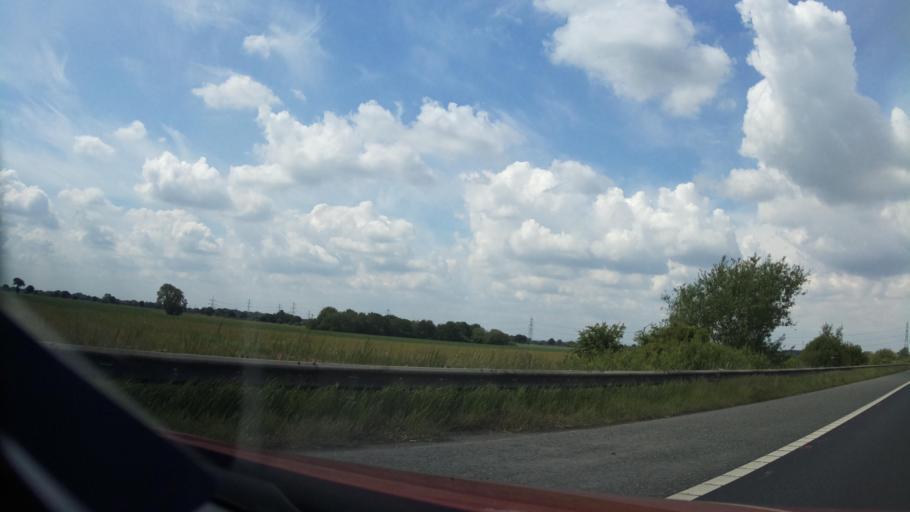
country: GB
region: England
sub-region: East Riding of Yorkshire
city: Snaith
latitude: 53.6786
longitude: -1.0332
